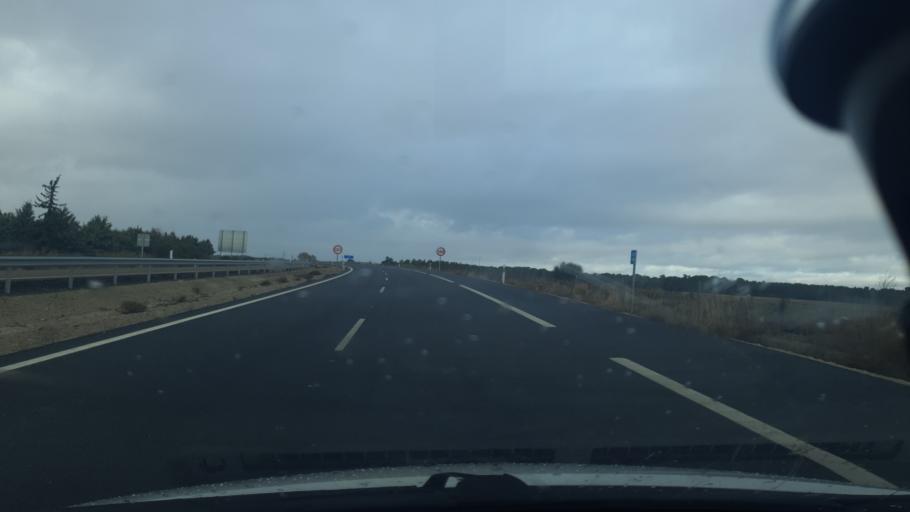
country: ES
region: Castille and Leon
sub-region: Provincia de Segovia
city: Cuellar
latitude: 41.4099
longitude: -4.3002
